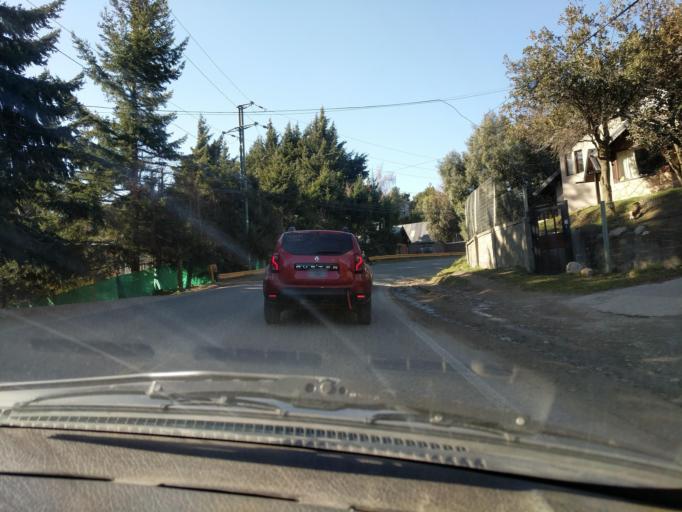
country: AR
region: Rio Negro
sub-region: Departamento de Bariloche
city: San Carlos de Bariloche
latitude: -41.1255
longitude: -71.3899
